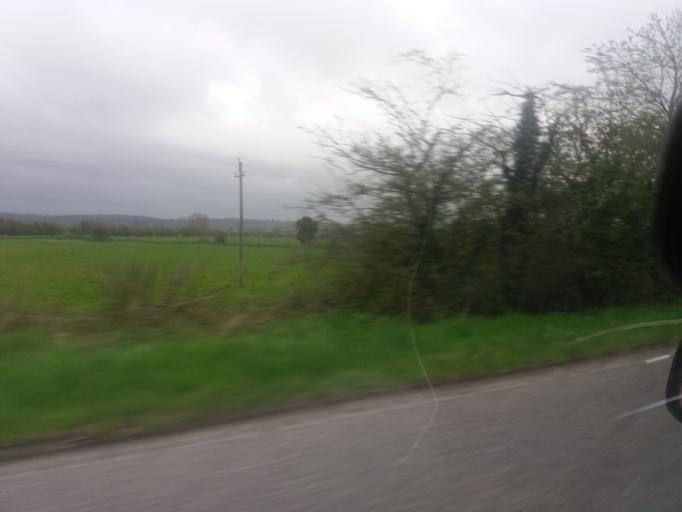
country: IE
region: Munster
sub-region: County Limerick
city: Rathkeale
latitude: 52.4932
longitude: -8.9995
